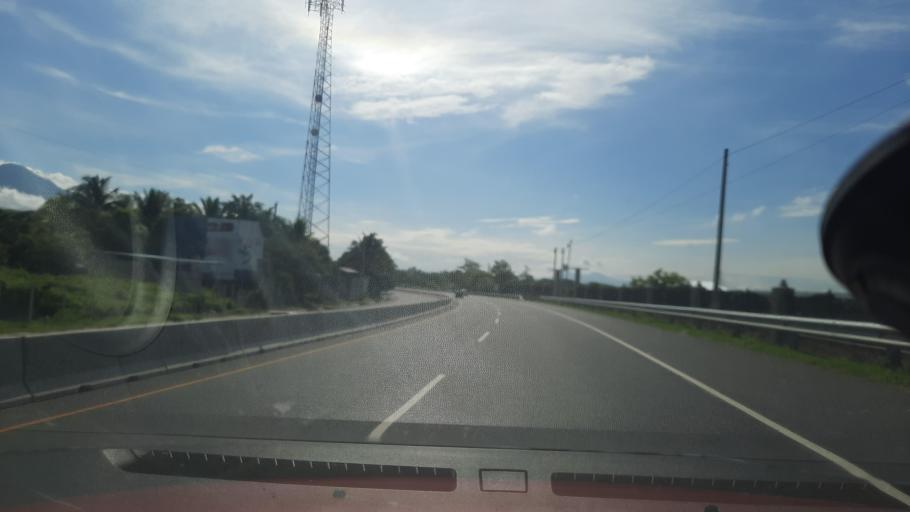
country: SV
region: La Paz
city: Santiago Nonualco
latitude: 13.4868
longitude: -88.9593
